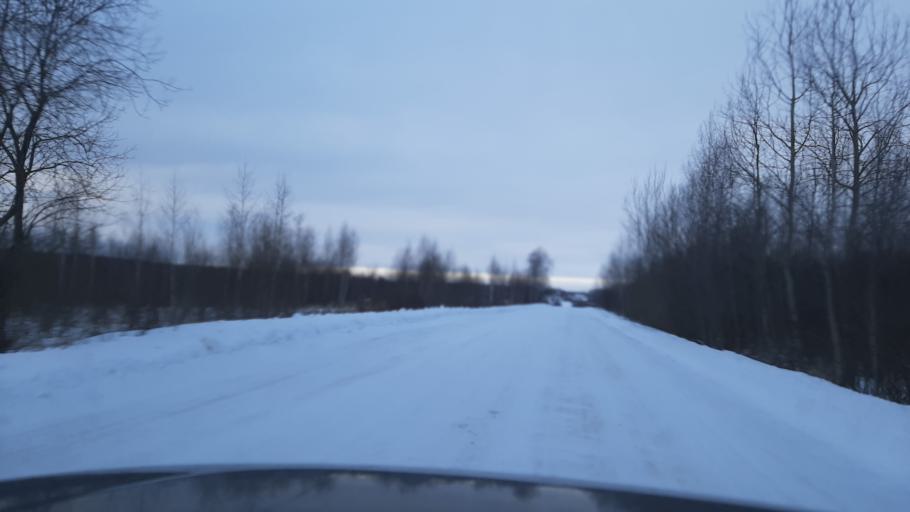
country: RU
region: Kostroma
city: Volgorechensk
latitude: 57.4476
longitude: 40.9918
